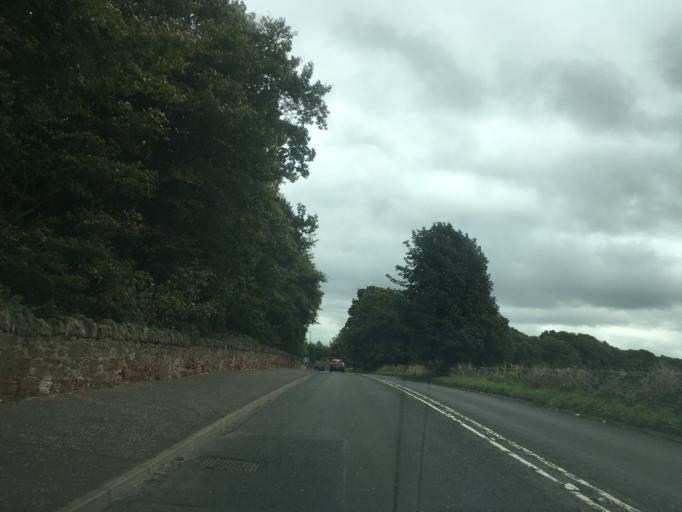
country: GB
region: Scotland
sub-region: Midlothian
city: Bonnyrigg
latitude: 55.8980
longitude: -3.1054
